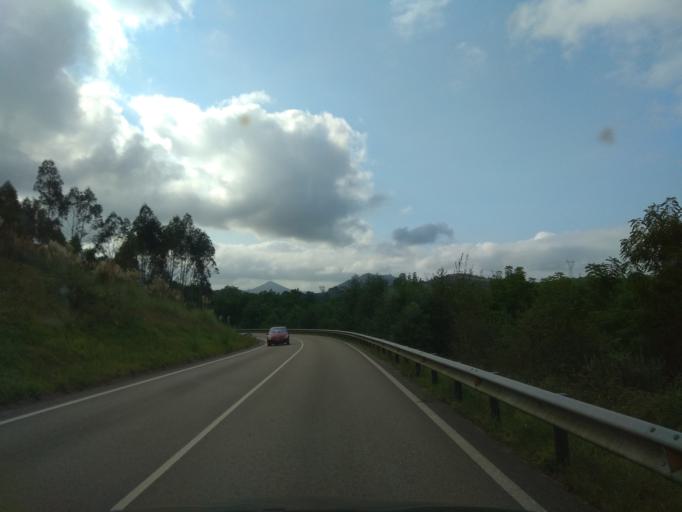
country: ES
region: Cantabria
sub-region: Provincia de Cantabria
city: Comillas
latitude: 43.3219
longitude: -4.3247
